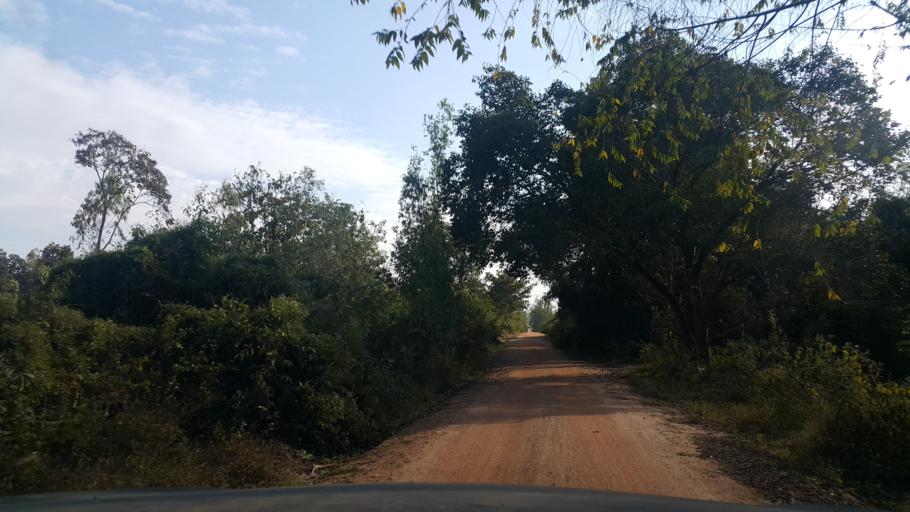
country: TH
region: Lampang
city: Hang Chat
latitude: 18.2961
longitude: 99.3528
